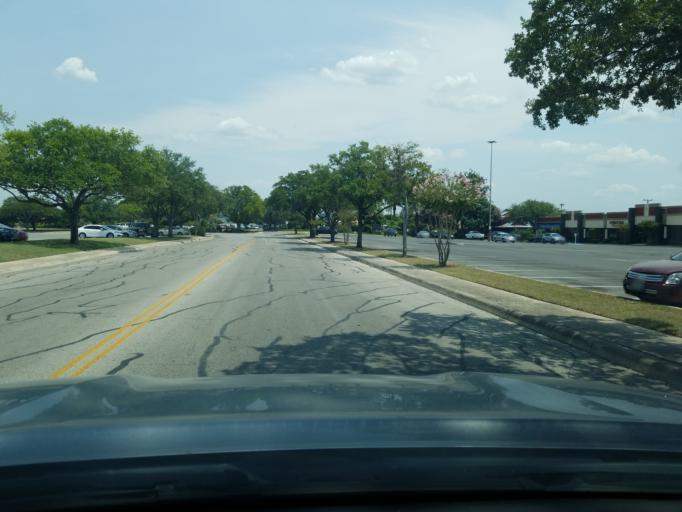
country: US
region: Texas
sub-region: Bexar County
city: Hollywood Park
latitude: 29.5642
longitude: -98.4876
